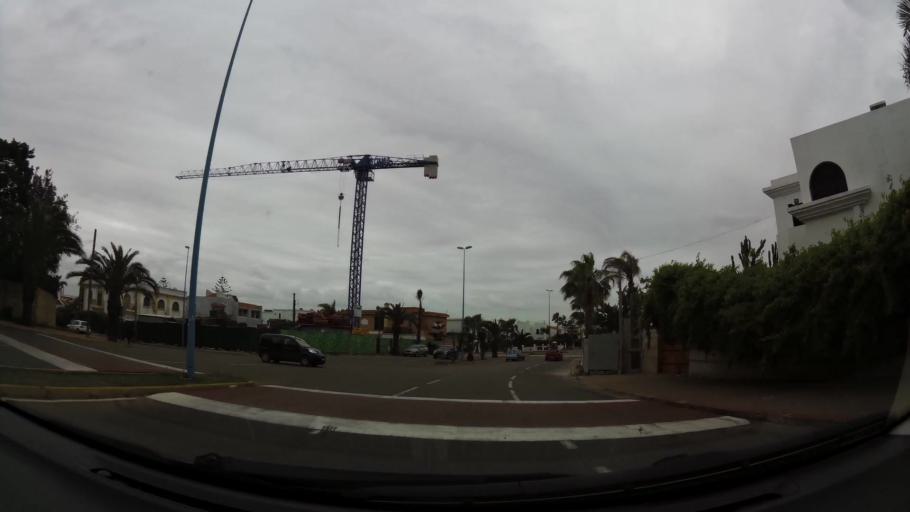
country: MA
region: Grand Casablanca
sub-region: Casablanca
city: Casablanca
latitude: 33.6022
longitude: -7.6558
